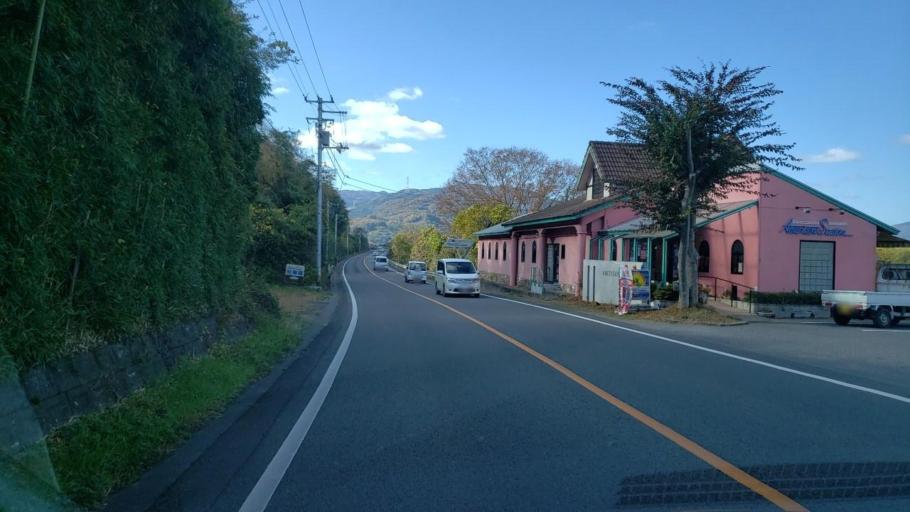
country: JP
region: Tokushima
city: Wakimachi
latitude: 34.0632
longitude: 134.1908
